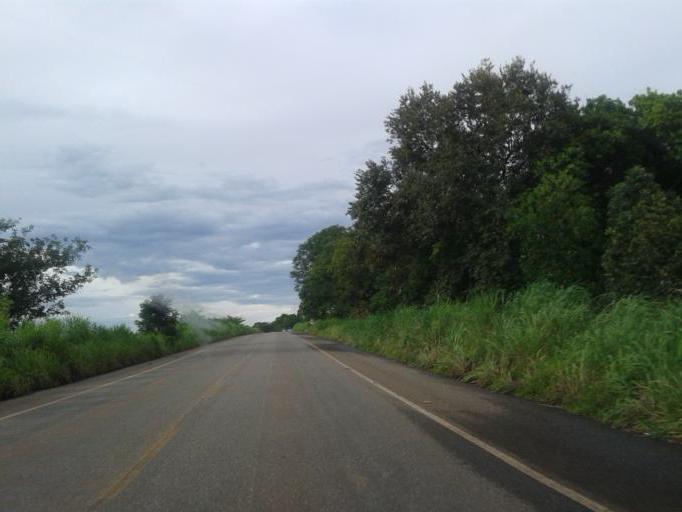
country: BR
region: Goias
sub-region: Mozarlandia
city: Mozarlandia
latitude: -14.7752
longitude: -50.5367
